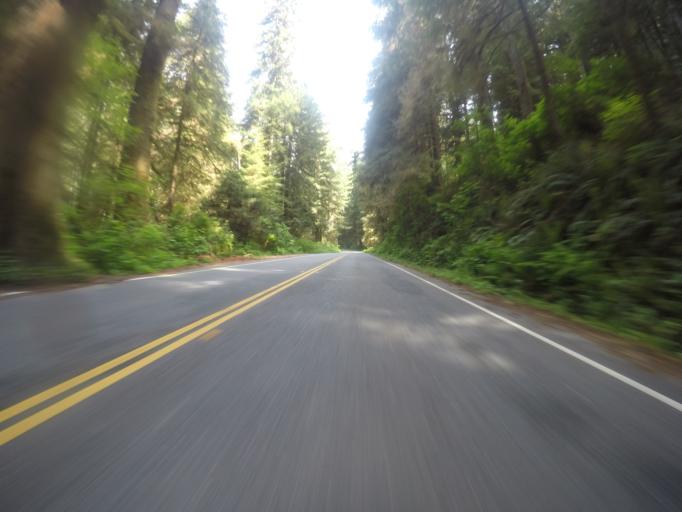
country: US
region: California
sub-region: Del Norte County
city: Bertsch-Oceanview
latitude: 41.4258
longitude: -124.0366
